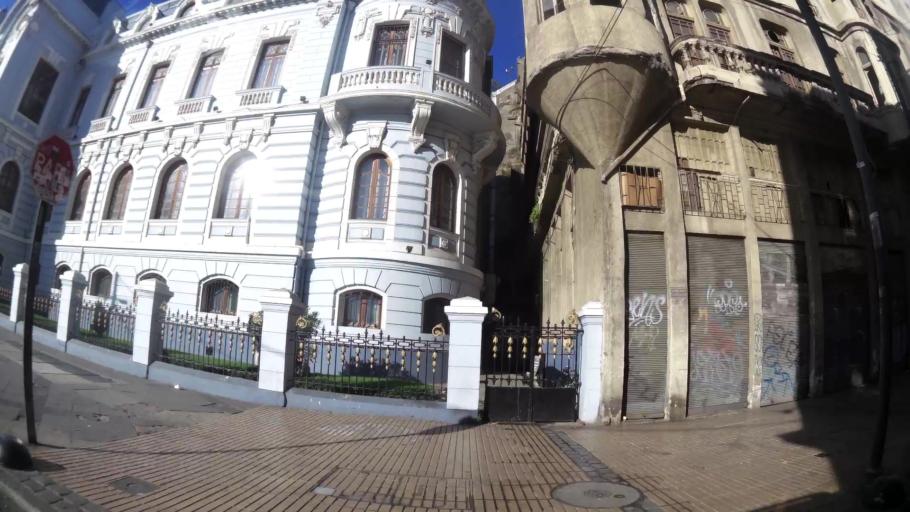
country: CL
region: Valparaiso
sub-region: Provincia de Valparaiso
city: Valparaiso
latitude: -33.0386
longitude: -71.6294
